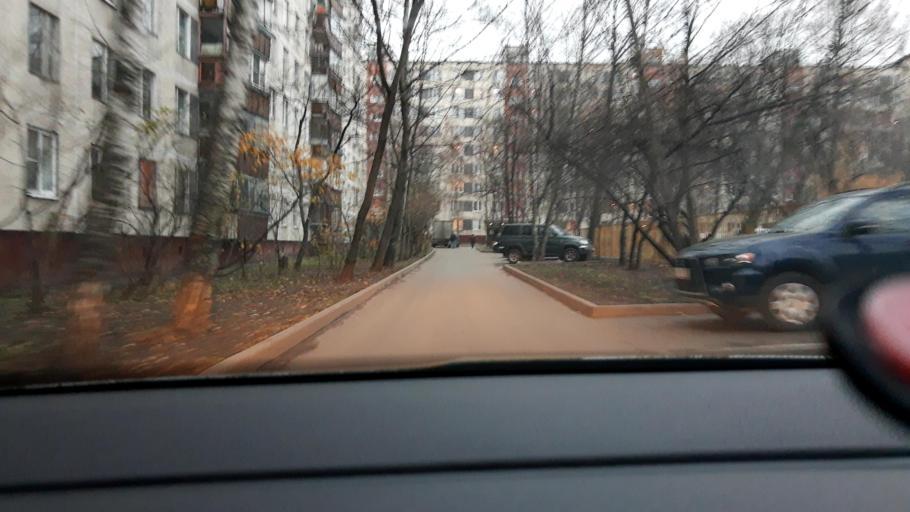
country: RU
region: Moscow
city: Bibirevo
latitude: 55.8951
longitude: 37.6070
